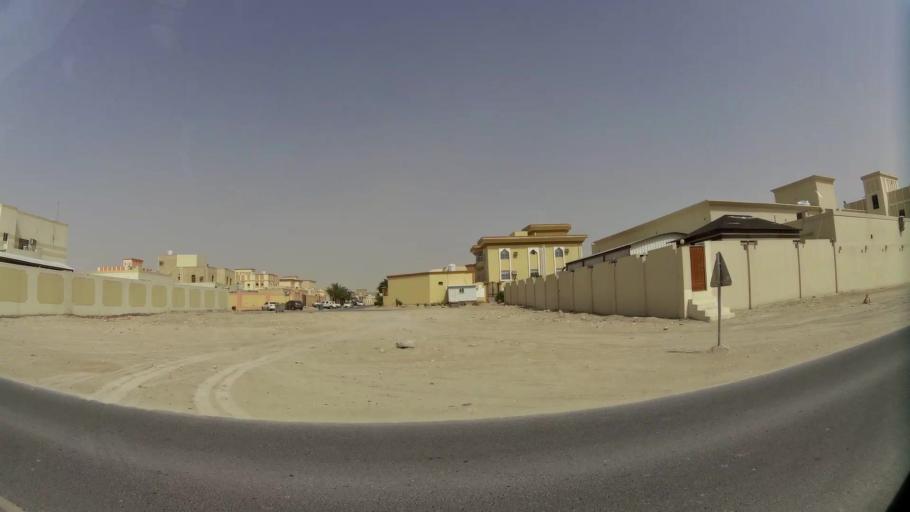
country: QA
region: Baladiyat ar Rayyan
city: Ar Rayyan
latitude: 25.2440
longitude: 51.3635
